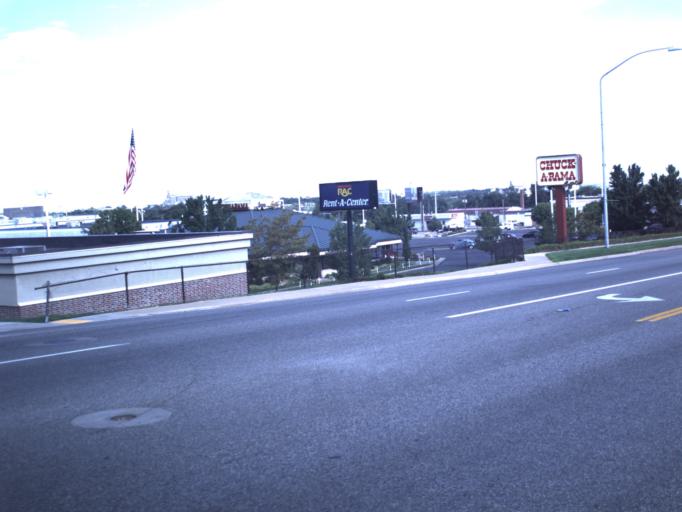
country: US
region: Utah
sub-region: Weber County
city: South Ogden
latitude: 41.1958
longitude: -111.9710
